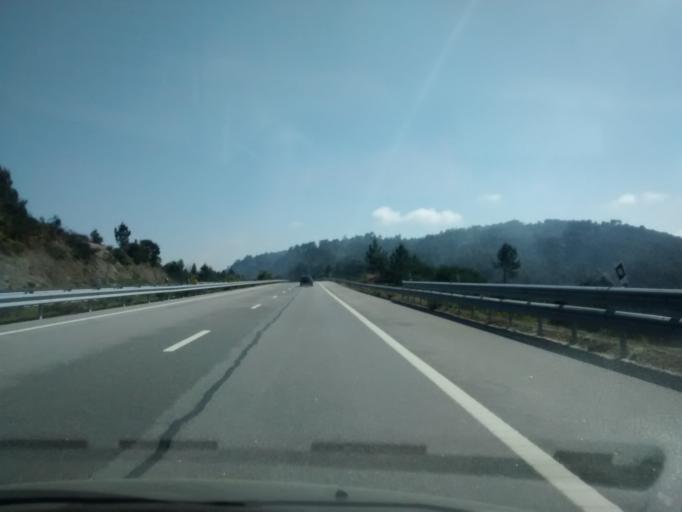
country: PT
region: Braga
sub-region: Cabeceiras de Basto
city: Refojos de Basto
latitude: 41.4644
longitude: -8.0127
